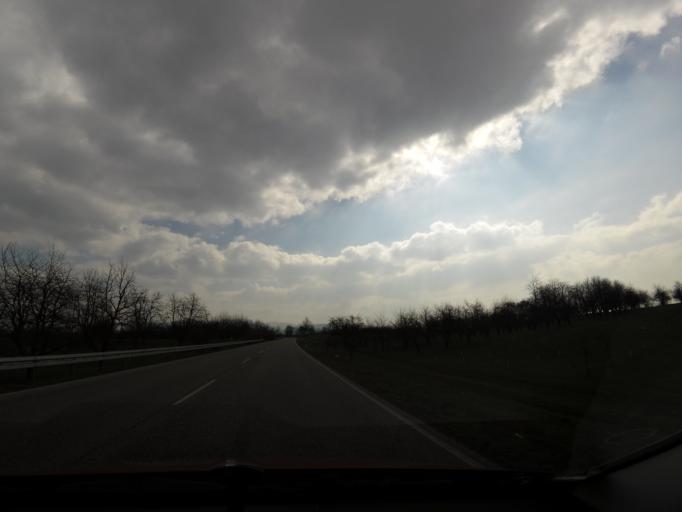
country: DE
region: Baden-Wuerttemberg
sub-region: Freiburg Region
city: Achern
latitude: 48.6174
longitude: 8.0668
